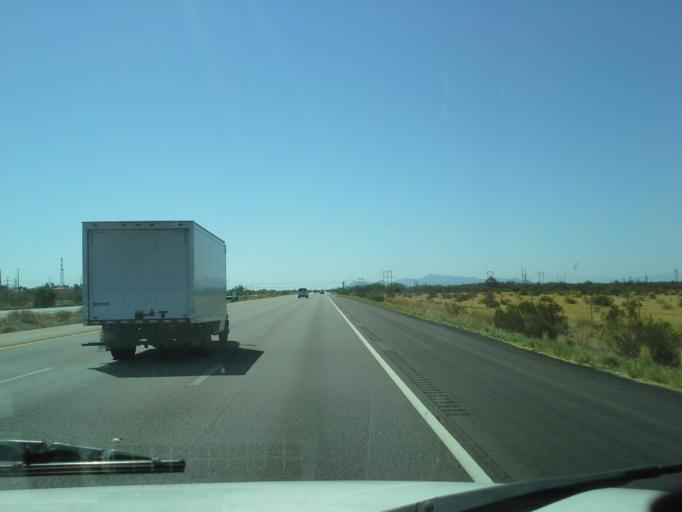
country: US
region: Arizona
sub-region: Pima County
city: Avra Valley
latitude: 32.5574
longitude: -111.3100
